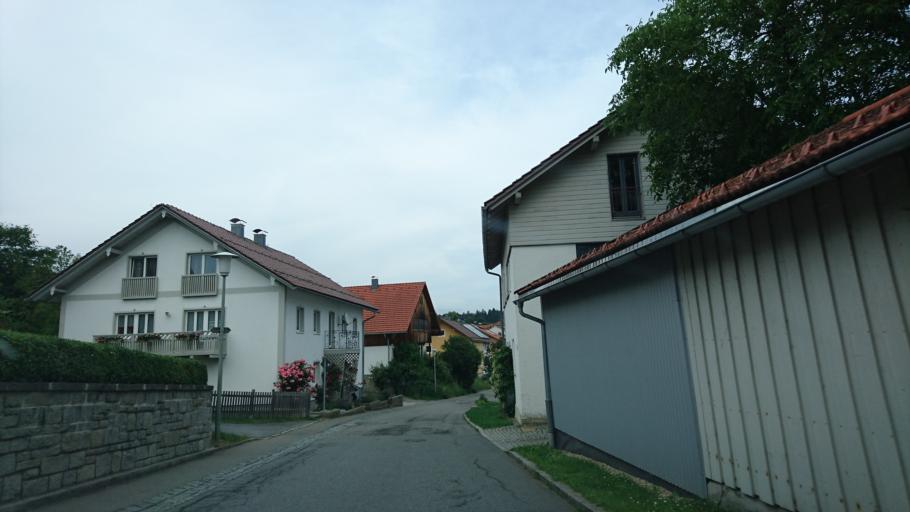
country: DE
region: Bavaria
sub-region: Lower Bavaria
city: Neuschonau
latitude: 48.8840
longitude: 13.4732
